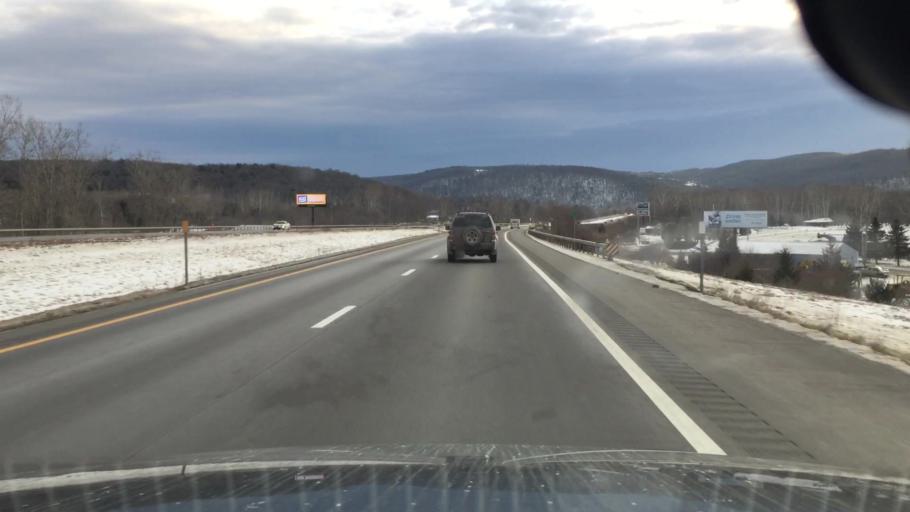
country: US
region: Pennsylvania
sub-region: Bradford County
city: Sayre
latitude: 42.0056
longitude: -76.4884
